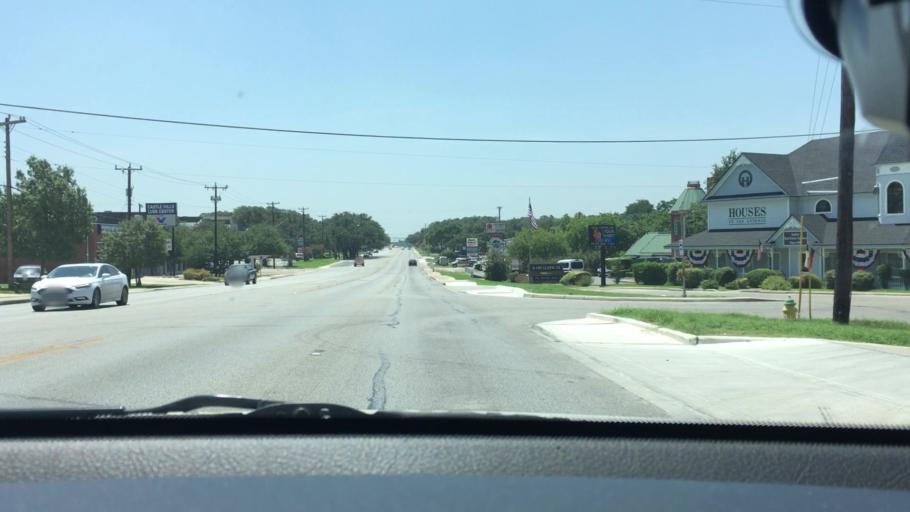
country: US
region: Texas
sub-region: Bexar County
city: Castle Hills
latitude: 29.5301
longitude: -98.5207
